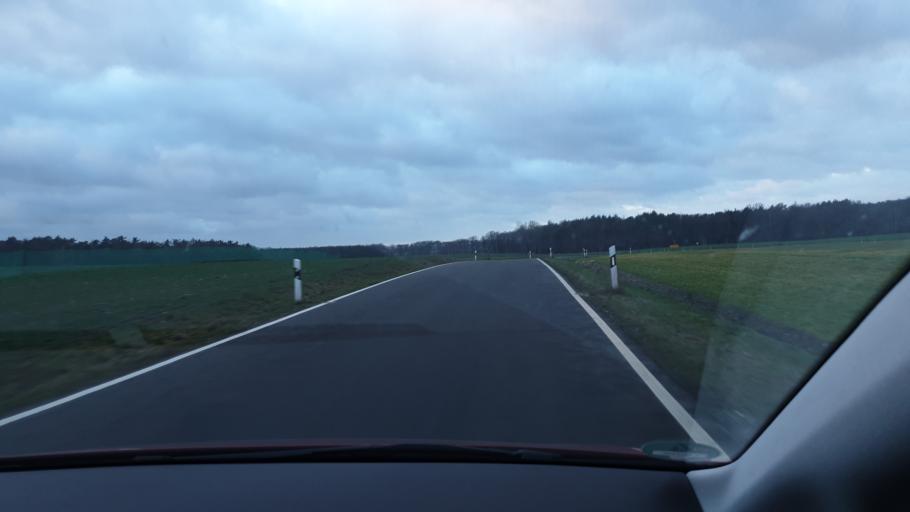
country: DE
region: Saxony
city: Falkenhain
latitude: 51.4523
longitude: 12.8593
